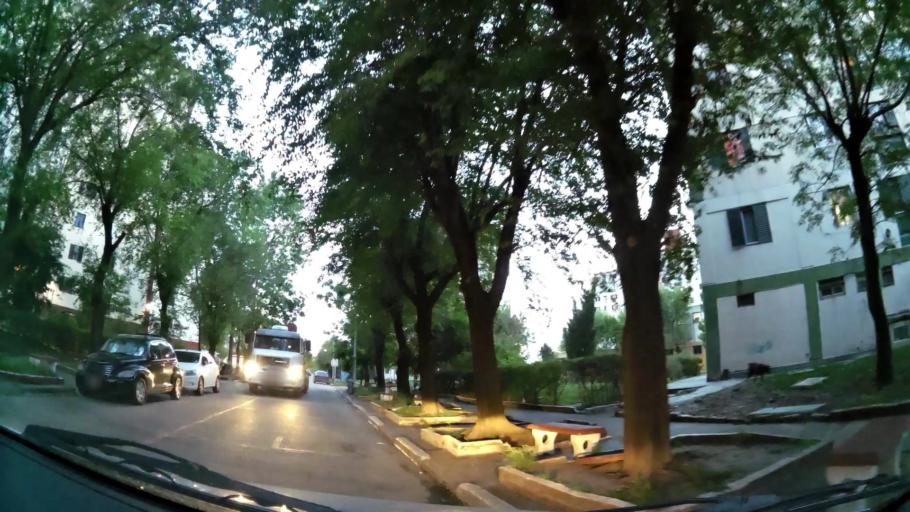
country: AR
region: Buenos Aires
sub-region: Partido de Avellaneda
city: Avellaneda
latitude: -34.6745
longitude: -58.3382
